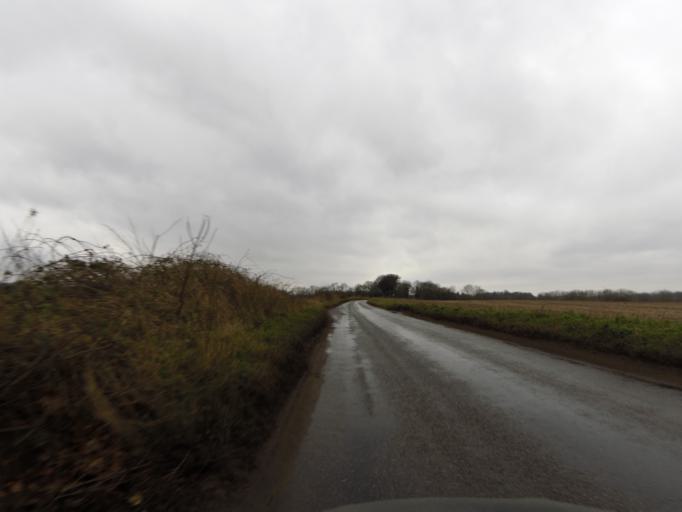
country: GB
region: England
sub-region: Norfolk
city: Briston
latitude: 52.7544
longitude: 1.1032
